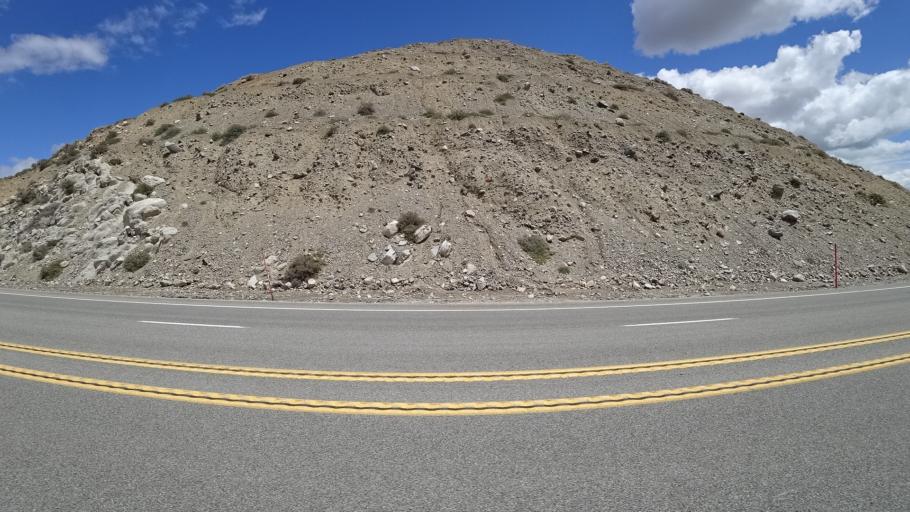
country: US
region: California
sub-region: Mono County
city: Bridgeport
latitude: 38.0753
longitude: -119.1784
